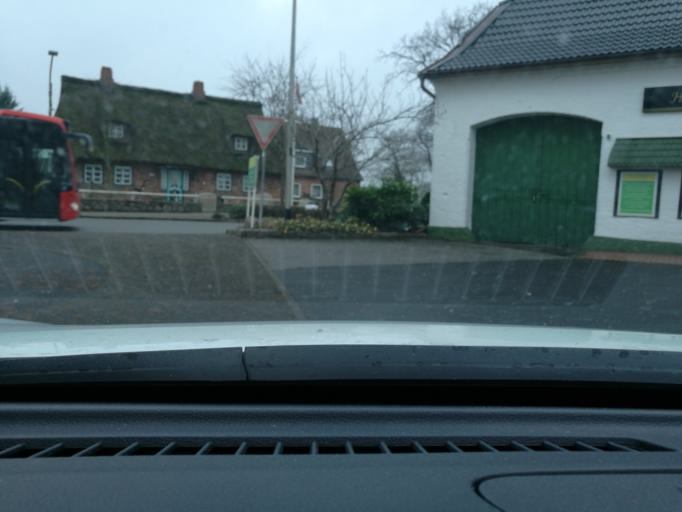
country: DE
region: Schleswig-Holstein
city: Borgstedt
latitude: 54.3331
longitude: 9.7101
